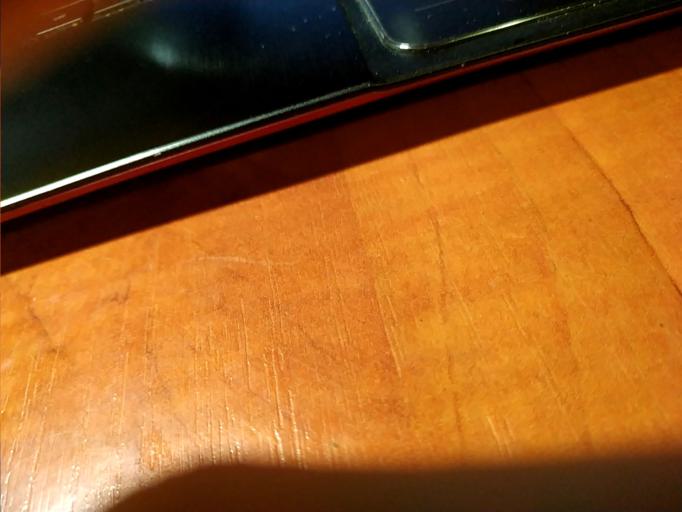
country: RU
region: Tverskaya
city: Ves'yegonsk
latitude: 58.7204
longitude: 37.5439
